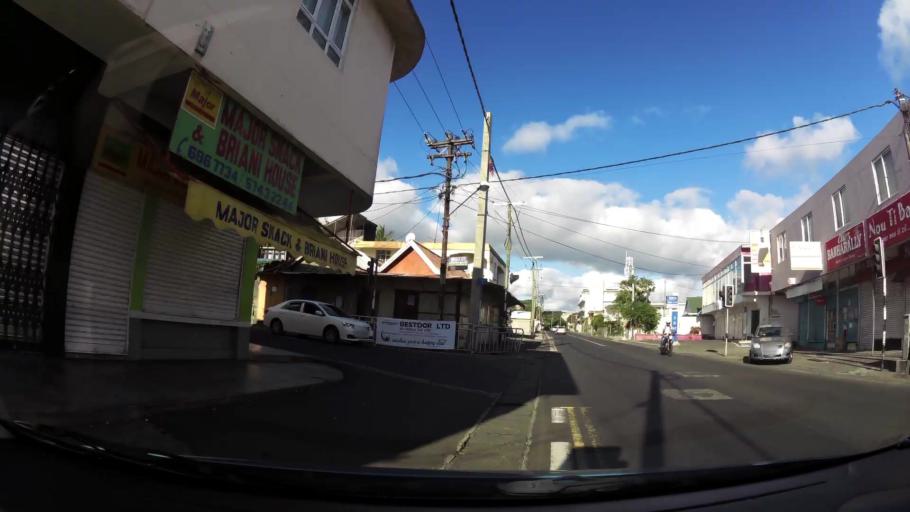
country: MU
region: Plaines Wilhems
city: Curepipe
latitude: -20.2914
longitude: 57.5148
